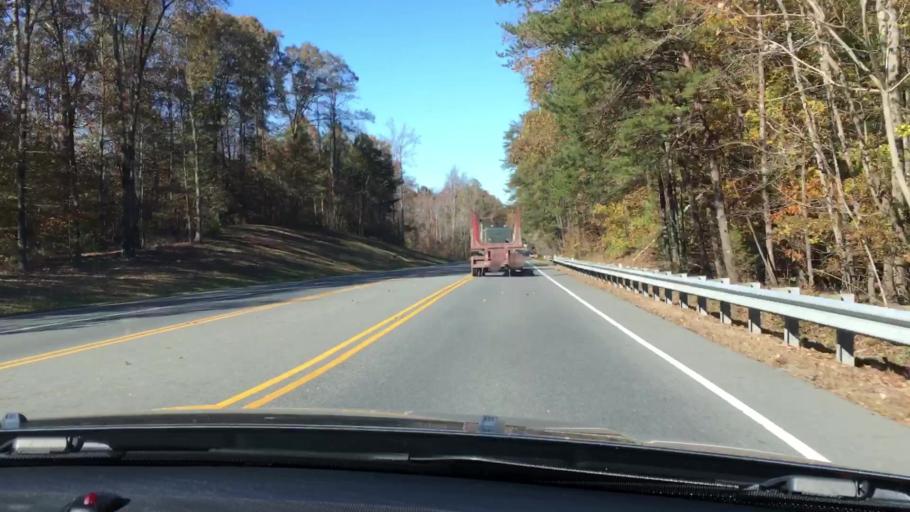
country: US
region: Virginia
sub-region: King William County
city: Central Garage
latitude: 37.7528
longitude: -77.1420
